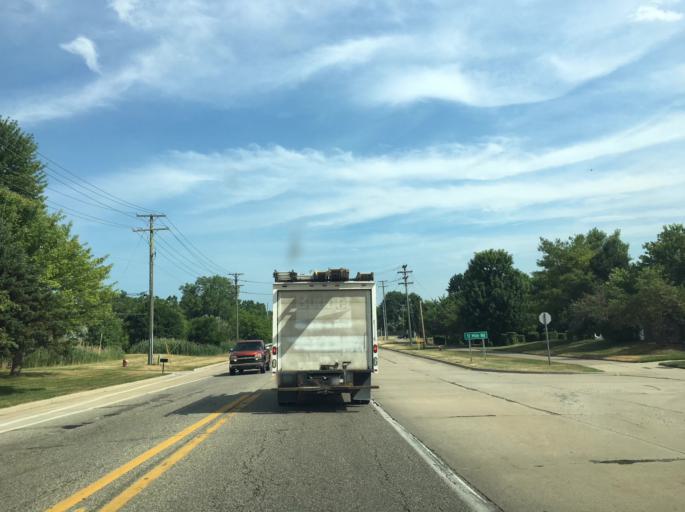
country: US
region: Michigan
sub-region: Macomb County
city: Sterling Heights
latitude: 42.5830
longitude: -82.9968
